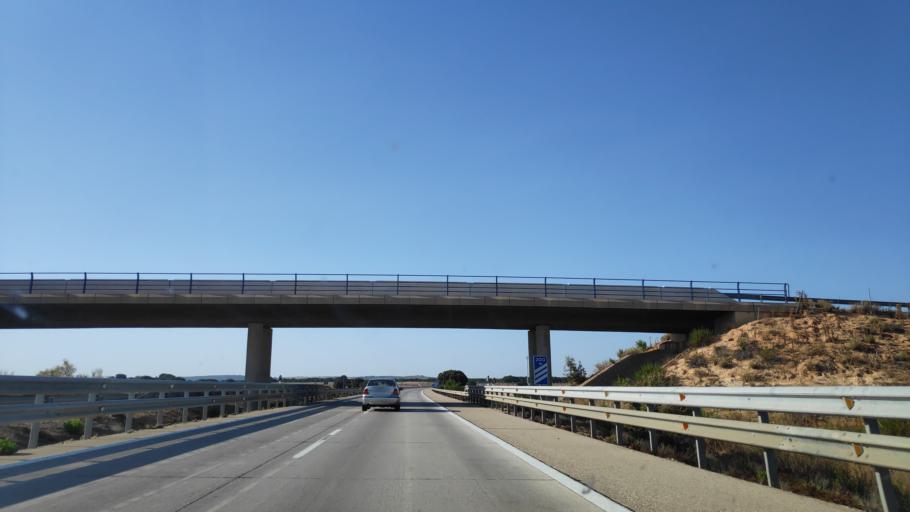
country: ES
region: Castille-La Mancha
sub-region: Provincia de Cuenca
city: Casas de Guijarro
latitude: 39.3147
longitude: -2.2035
